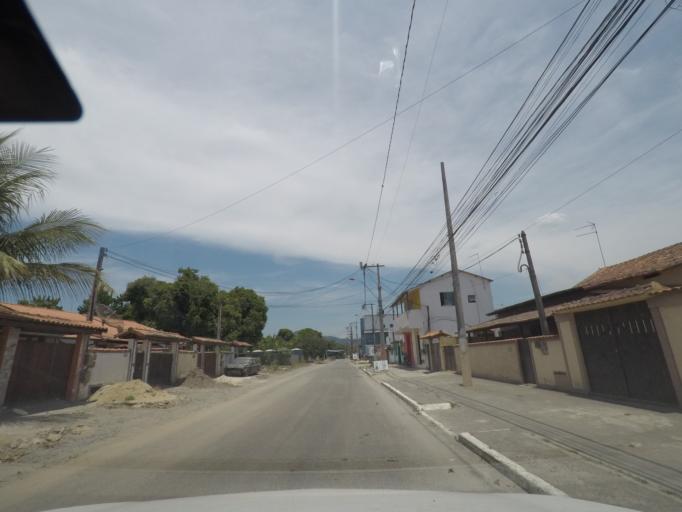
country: BR
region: Rio de Janeiro
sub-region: Marica
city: Marica
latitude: -22.9091
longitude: -42.8336
